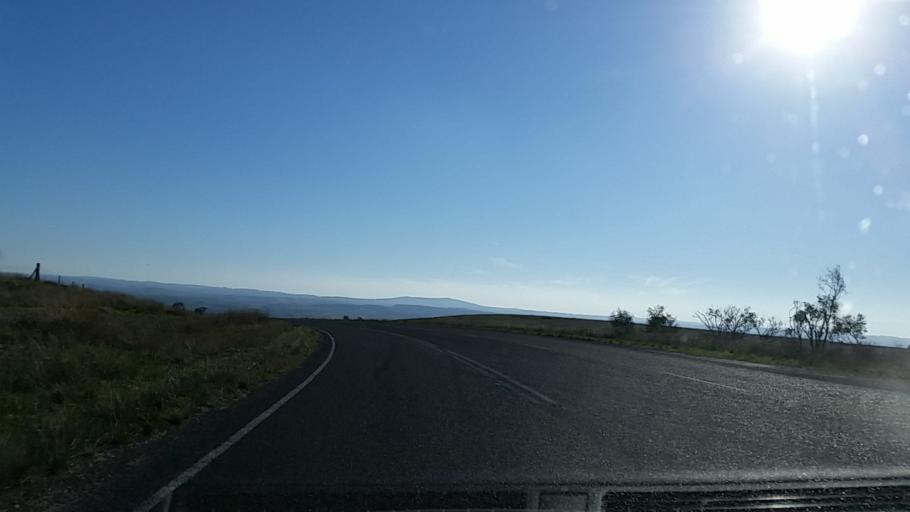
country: AU
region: South Australia
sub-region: Mount Barker
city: Callington
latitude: -35.1112
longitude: 139.0768
